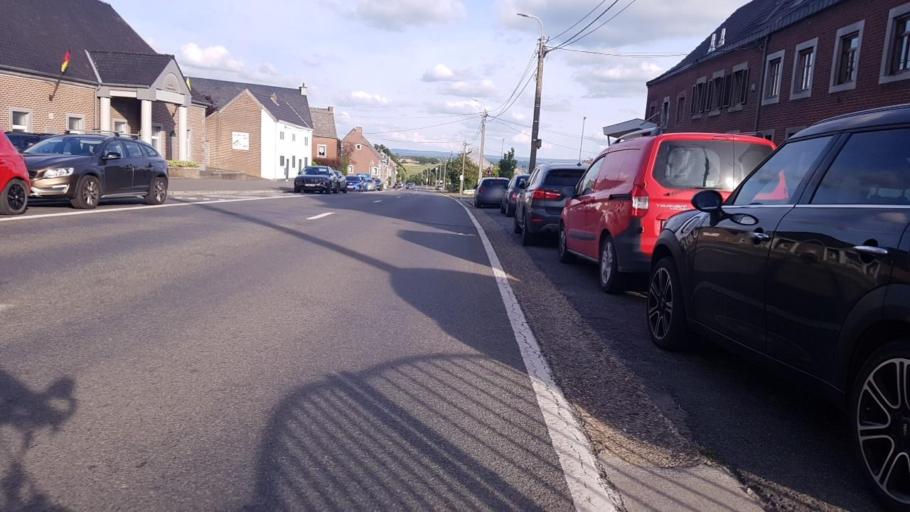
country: BE
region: Wallonia
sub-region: Province de Liege
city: Soumagne
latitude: 50.6087
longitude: 5.7140
